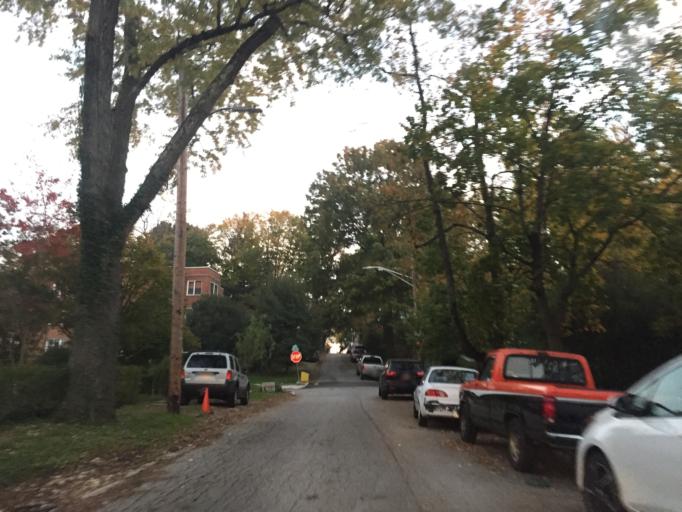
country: US
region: Maryland
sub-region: Baltimore County
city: Towson
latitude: 39.3562
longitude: -76.6323
